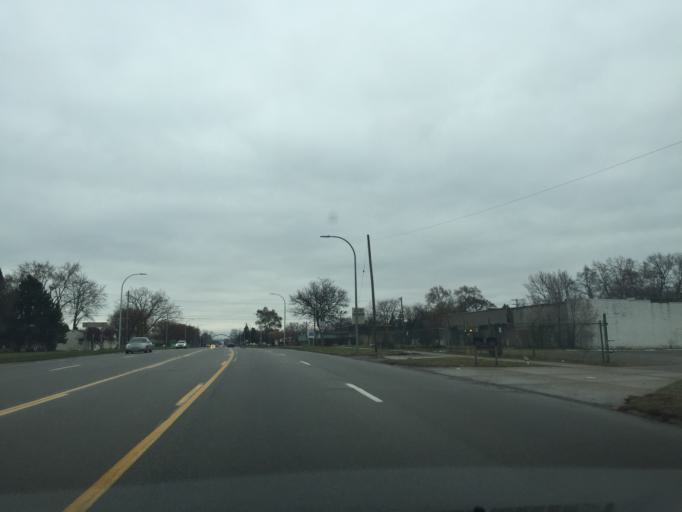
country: US
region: Michigan
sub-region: Oakland County
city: Farmington
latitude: 42.4409
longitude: -83.3366
